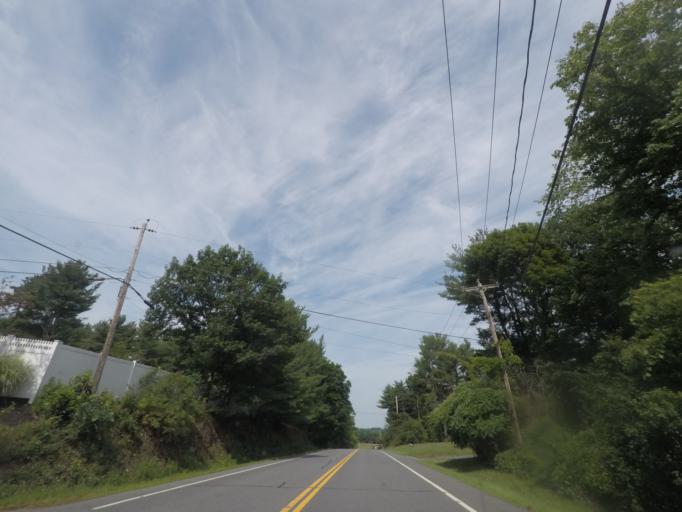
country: US
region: New York
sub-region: Rensselaer County
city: Wynantskill
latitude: 42.7301
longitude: -73.6108
